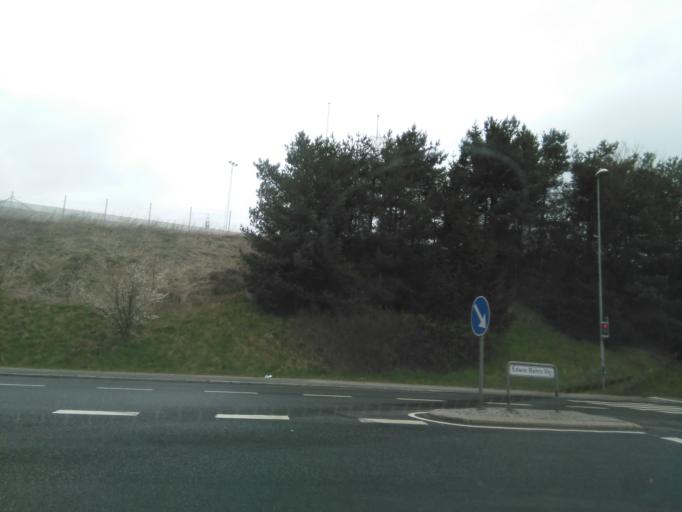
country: DK
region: Central Jutland
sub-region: Arhus Kommune
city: Stavtrup
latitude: 56.1644
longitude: 10.1008
